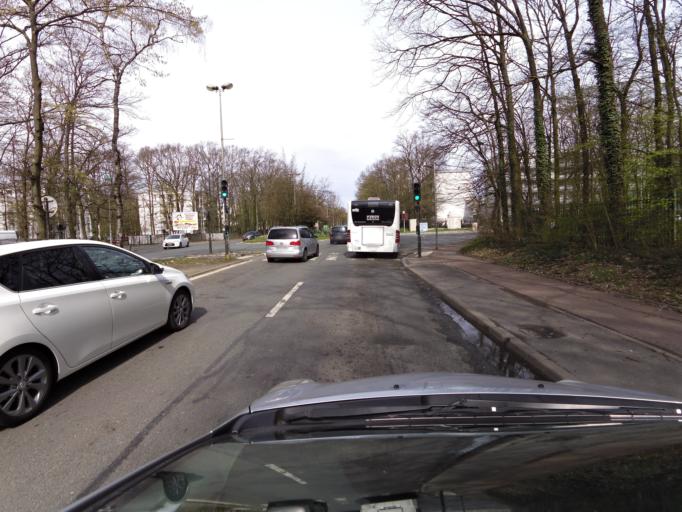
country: FR
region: Ile-de-France
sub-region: Departement de Seine-Saint-Denis
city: Tremblay-en-France
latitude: 48.9470
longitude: 2.5669
